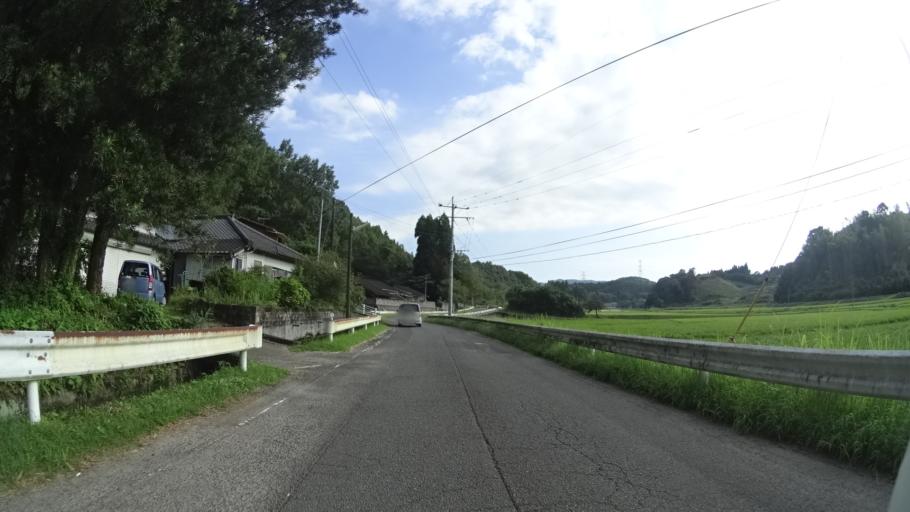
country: JP
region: Kagoshima
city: Okuchi-shinohara
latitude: 32.0206
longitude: 130.6624
